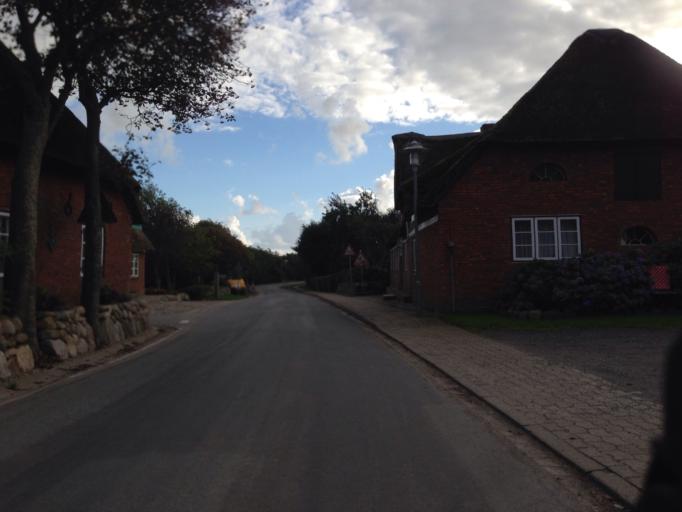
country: DE
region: Schleswig-Holstein
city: Suderende
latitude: 54.7255
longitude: 8.4393
